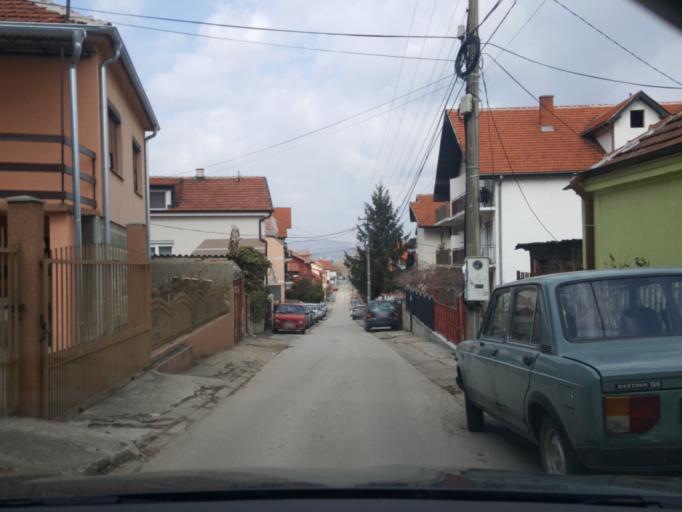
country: RS
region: Central Serbia
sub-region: Nisavski Okrug
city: Nis
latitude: 43.3124
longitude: 21.8653
